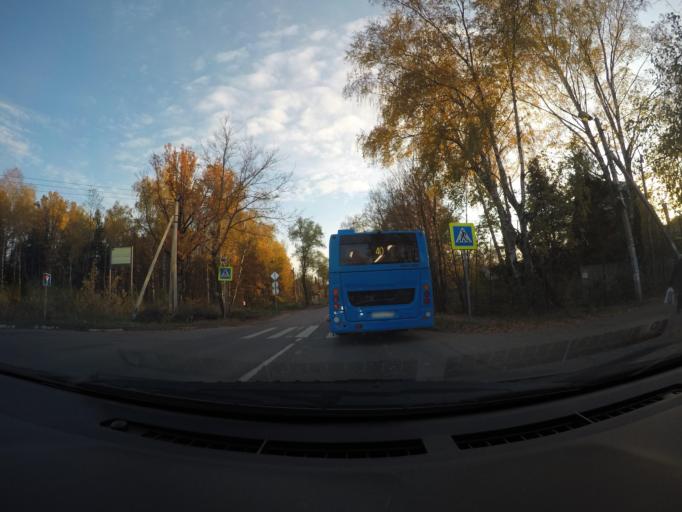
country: RU
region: Moskovskaya
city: Firsanovka
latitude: 55.9481
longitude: 37.2511
